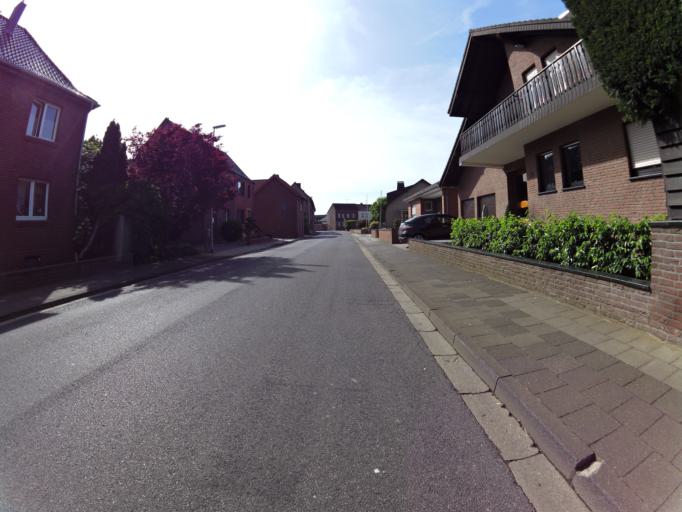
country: DE
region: North Rhine-Westphalia
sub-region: Regierungsbezirk Koln
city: Heinsberg
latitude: 51.0157
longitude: 6.0733
